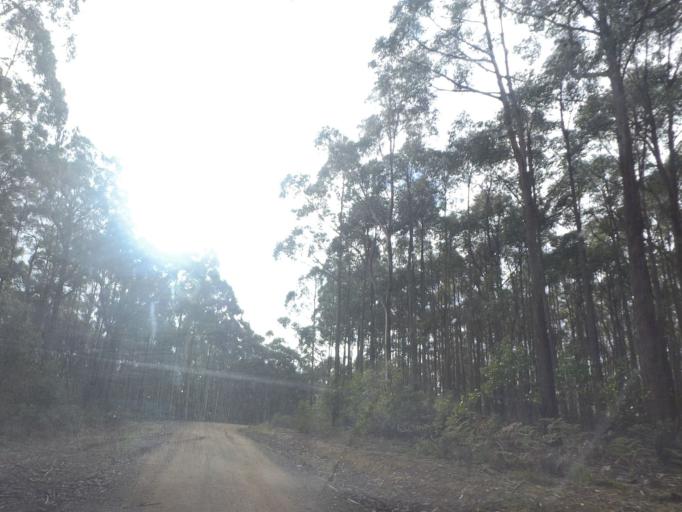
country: AU
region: Victoria
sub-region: Moorabool
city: Bacchus Marsh
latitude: -37.4234
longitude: 144.4169
